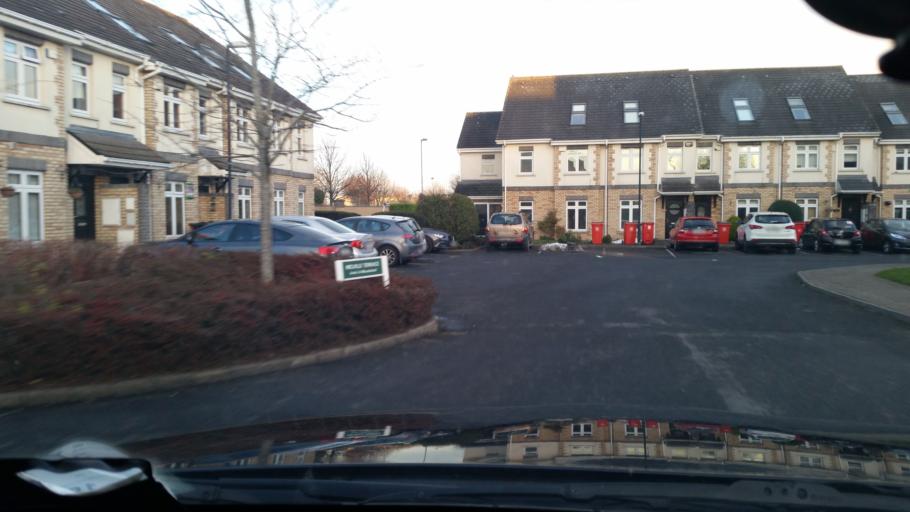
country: IE
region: Leinster
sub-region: Dublin City
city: Finglas
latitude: 53.4007
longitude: -6.2922
